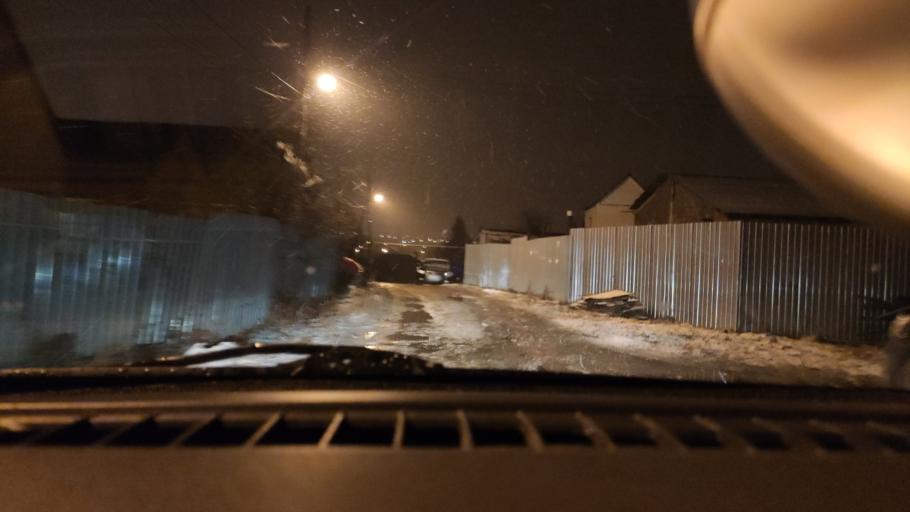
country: RU
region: Samara
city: Samara
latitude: 53.1719
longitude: 50.1702
